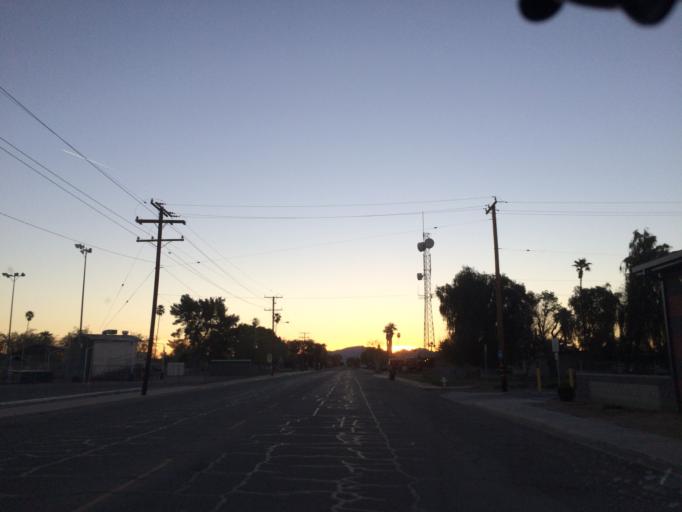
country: US
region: California
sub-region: Riverside County
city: Blythe
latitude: 33.6139
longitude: -114.5994
